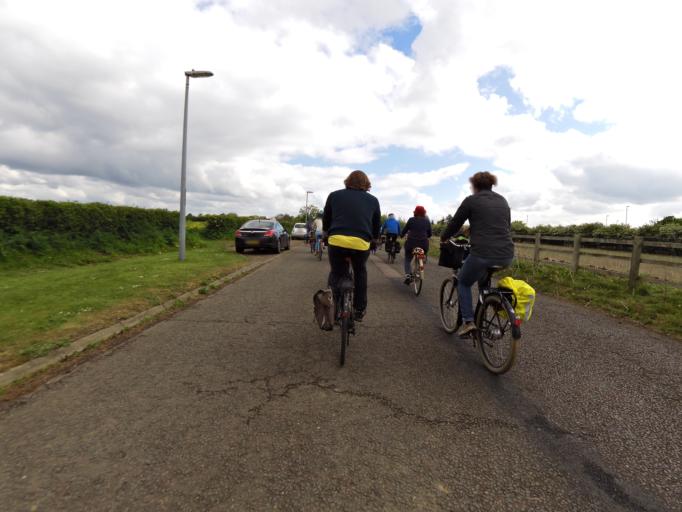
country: GB
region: England
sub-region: Cambridgeshire
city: Fulbourn
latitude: 52.2150
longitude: 0.2141
